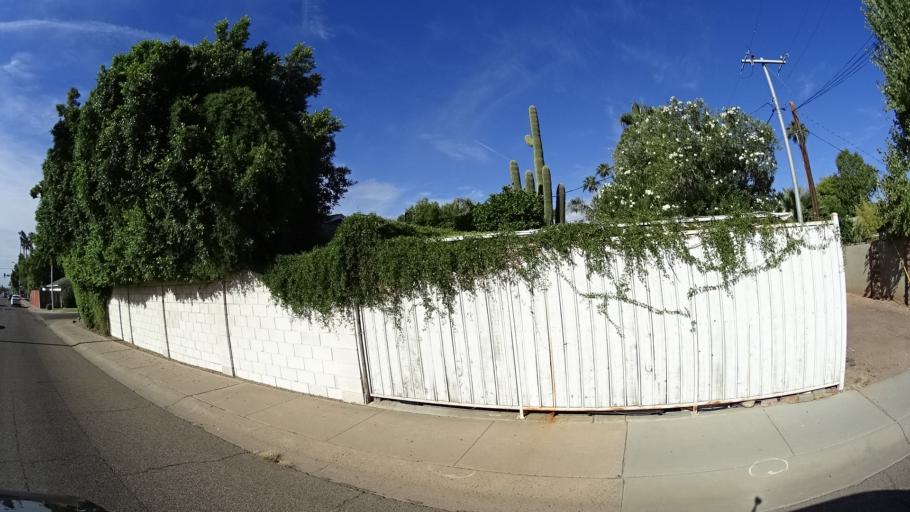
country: US
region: Arizona
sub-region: Maricopa County
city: Scottsdale
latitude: 33.4887
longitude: -111.9348
